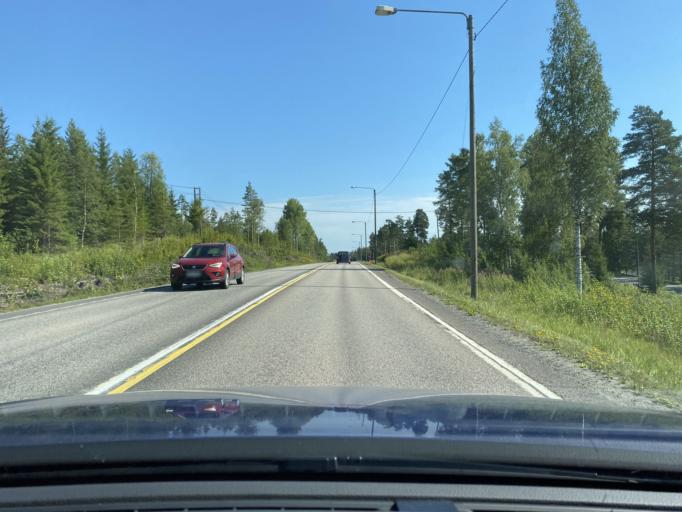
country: FI
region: Central Finland
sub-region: Jaemsae
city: Jaemsae
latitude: 61.8713
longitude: 25.2371
